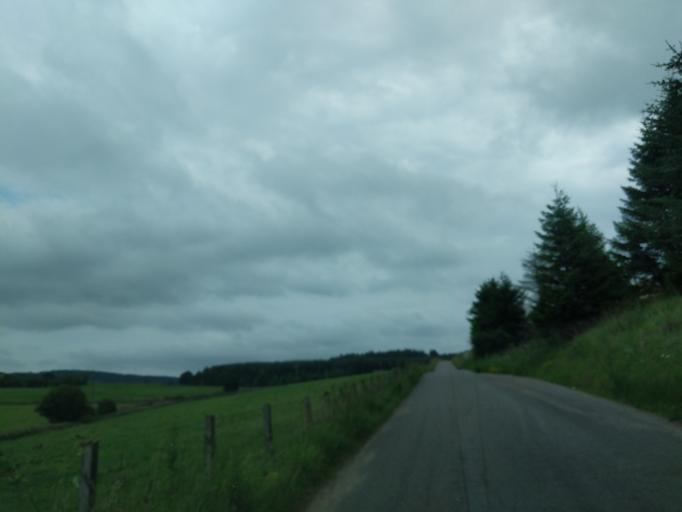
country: GB
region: Scotland
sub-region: Moray
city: Rothes
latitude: 57.4891
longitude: -3.2214
